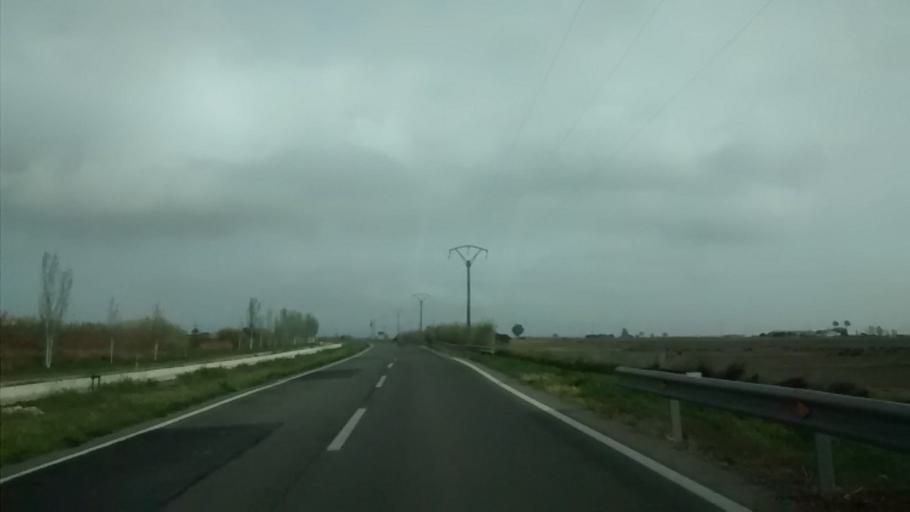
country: ES
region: Catalonia
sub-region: Provincia de Tarragona
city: Sant Carles de la Rapita
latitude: 40.6341
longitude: 0.6017
